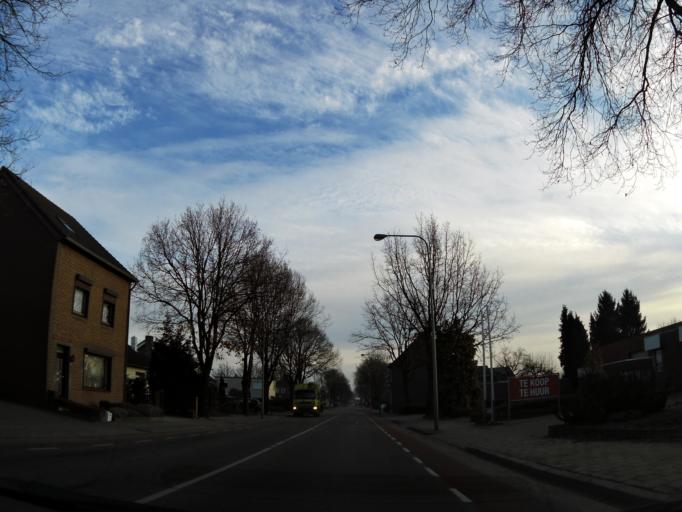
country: NL
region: Limburg
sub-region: Gemeente Heerlen
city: Heerlen
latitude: 50.9209
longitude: 6.0285
